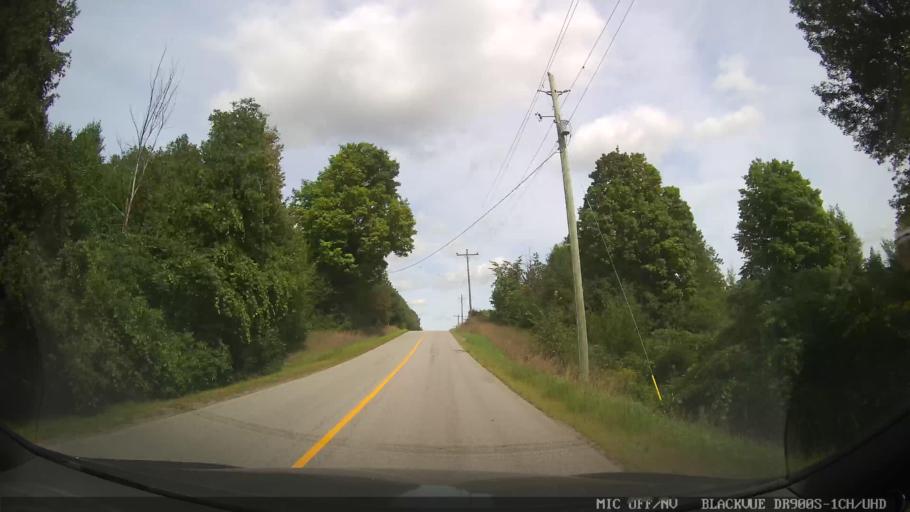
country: CA
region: Ontario
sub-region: Lanark County
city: Smiths Falls
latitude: 44.9064
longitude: -75.9011
